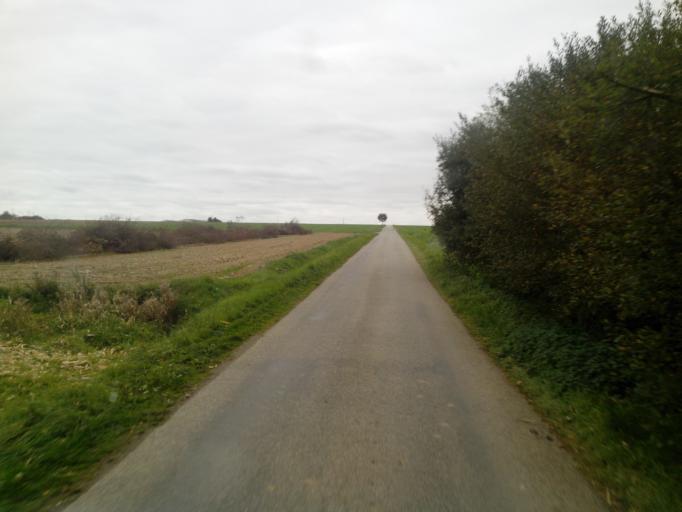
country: FR
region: Brittany
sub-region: Departement du Morbihan
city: Mauron
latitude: 48.0811
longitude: -2.3165
